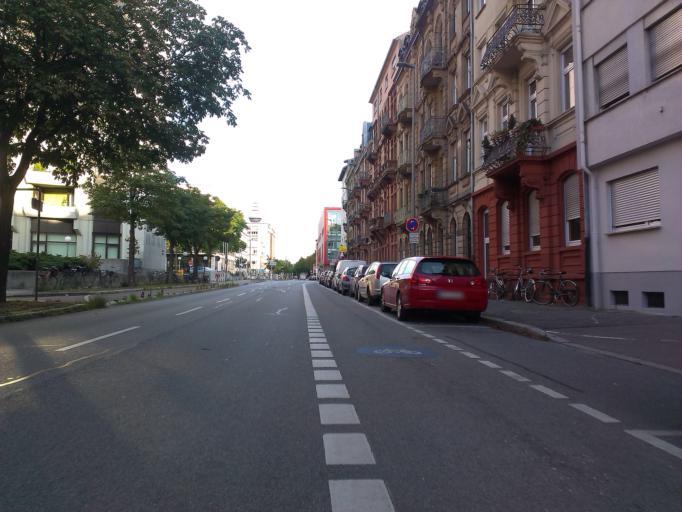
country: DE
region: Baden-Wuerttemberg
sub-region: Karlsruhe Region
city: Mannheim
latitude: 49.4905
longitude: 8.4768
